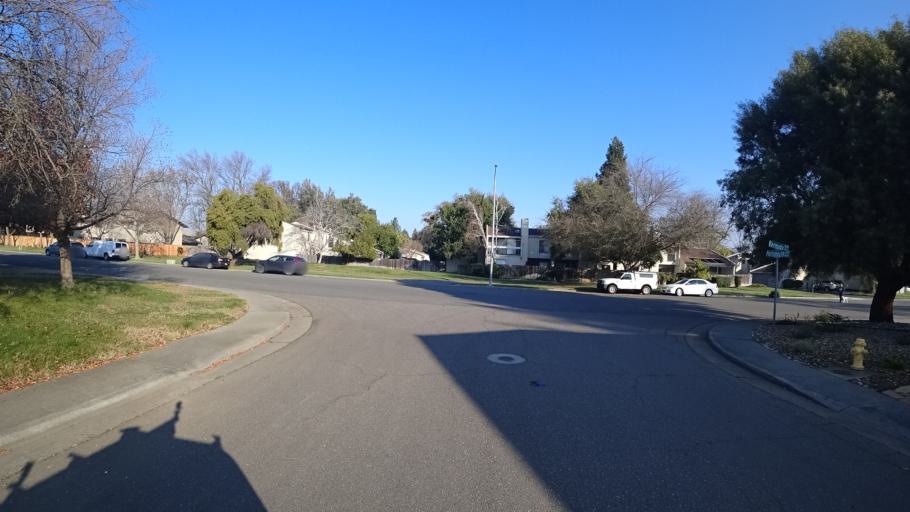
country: US
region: California
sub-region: Yolo County
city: Davis
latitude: 38.5497
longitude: -121.7926
